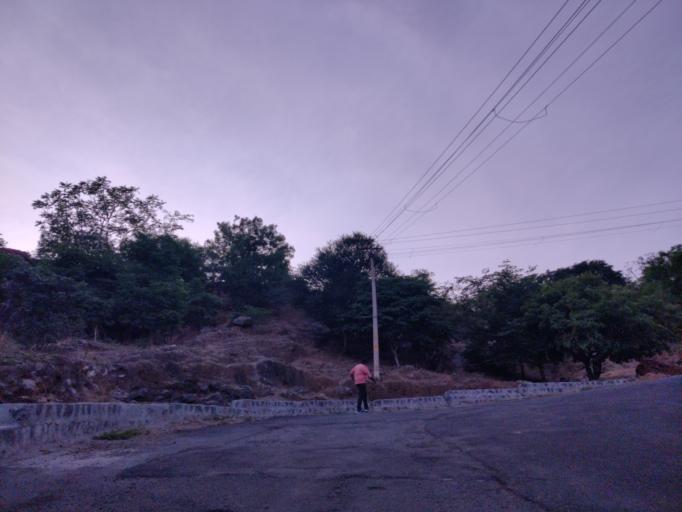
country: IN
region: Tamil Nadu
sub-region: Salem
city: Salem
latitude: 11.6218
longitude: 78.1503
